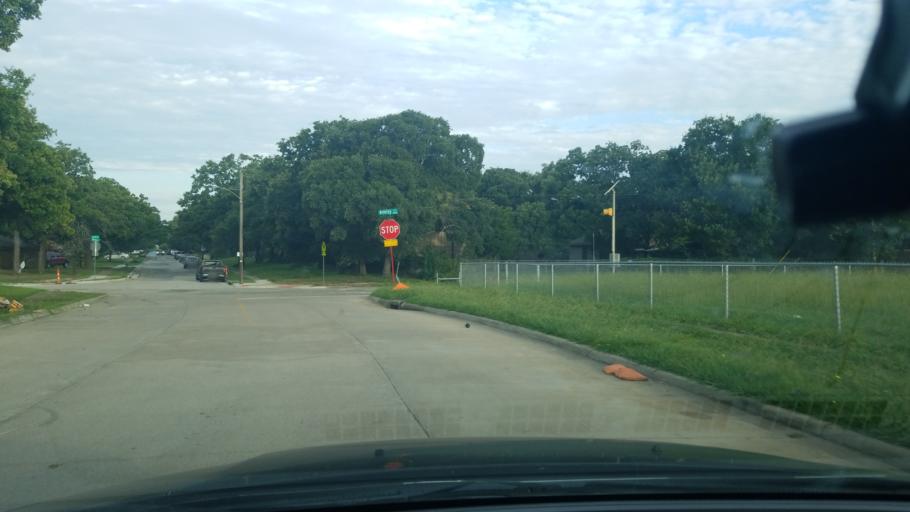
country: US
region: Texas
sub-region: Dallas County
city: Balch Springs
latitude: 32.7399
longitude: -96.6422
